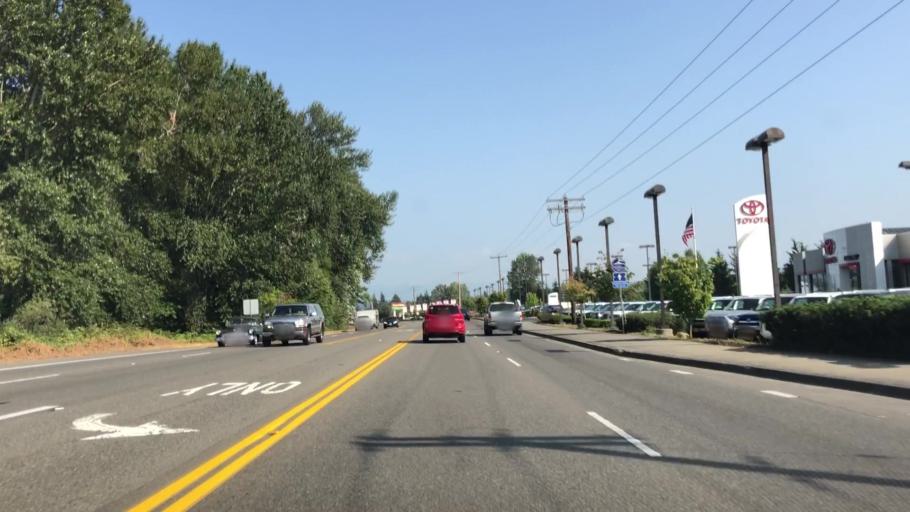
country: US
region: Washington
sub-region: Pierce County
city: Puyallup
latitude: 47.2042
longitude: -122.3133
